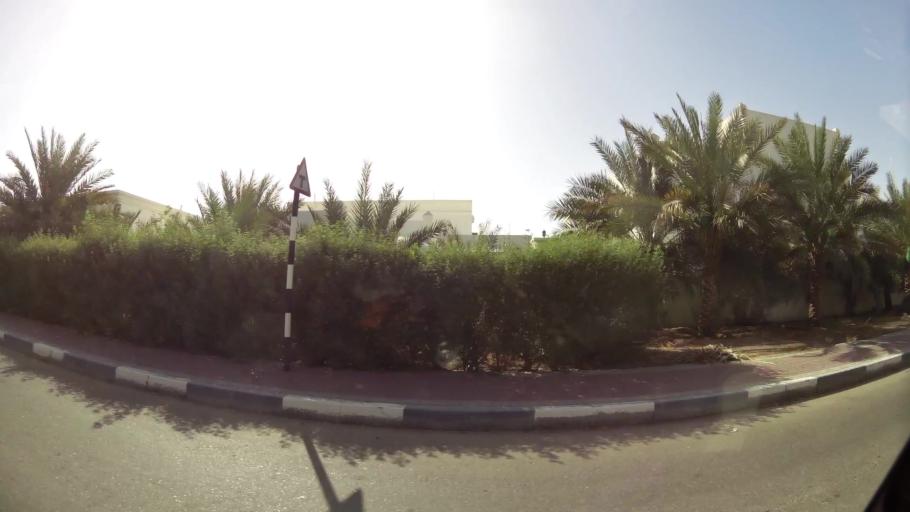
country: OM
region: Al Buraimi
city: Al Buraymi
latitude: 24.3463
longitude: 55.7987
